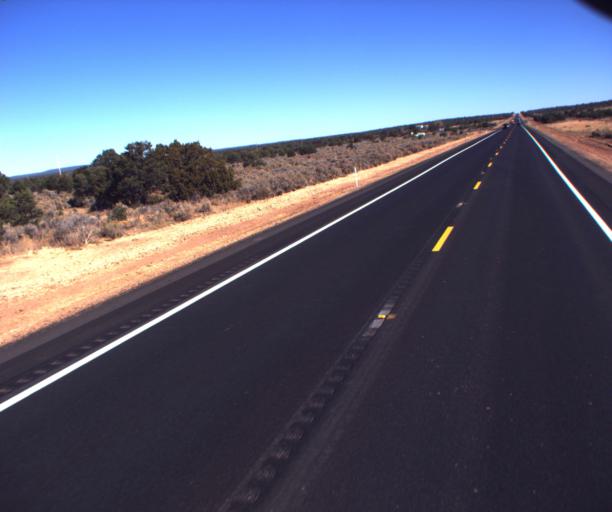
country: US
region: Arizona
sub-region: Apache County
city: Ganado
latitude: 35.7174
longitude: -109.4066
